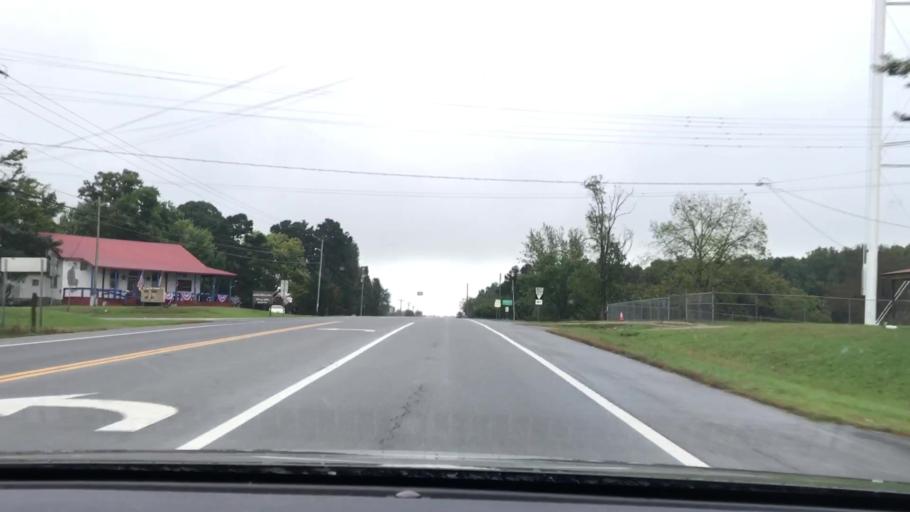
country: US
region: Tennessee
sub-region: Fentress County
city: Grimsley
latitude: 36.2445
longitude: -85.0024
